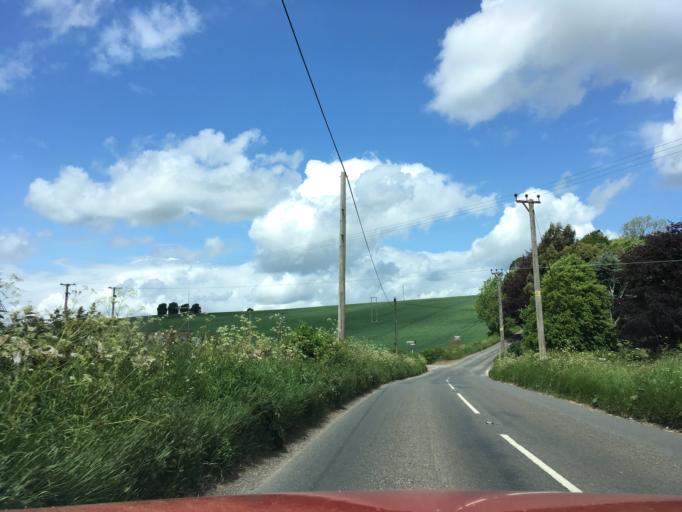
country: GB
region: England
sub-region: Gloucestershire
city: Chalford
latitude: 51.7857
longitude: -2.1293
